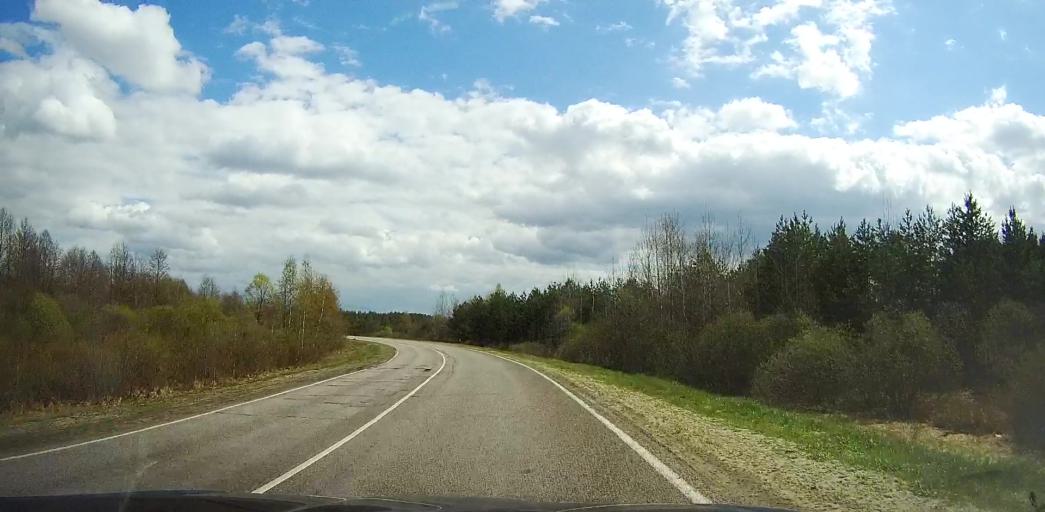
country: RU
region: Moskovskaya
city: Davydovo
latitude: 55.5476
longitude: 38.8103
